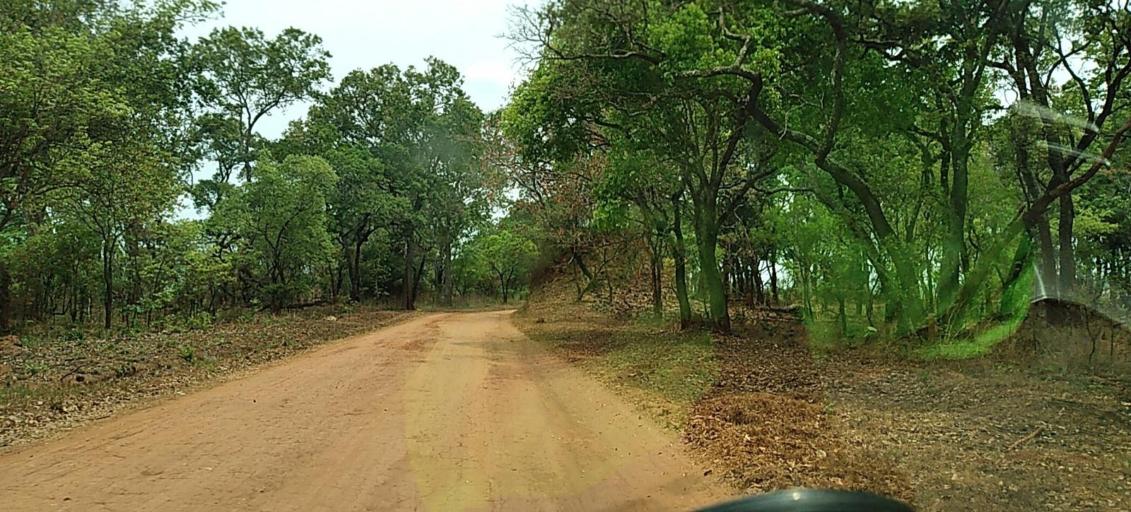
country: ZM
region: North-Western
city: Solwezi
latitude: -12.8095
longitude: 26.5379
